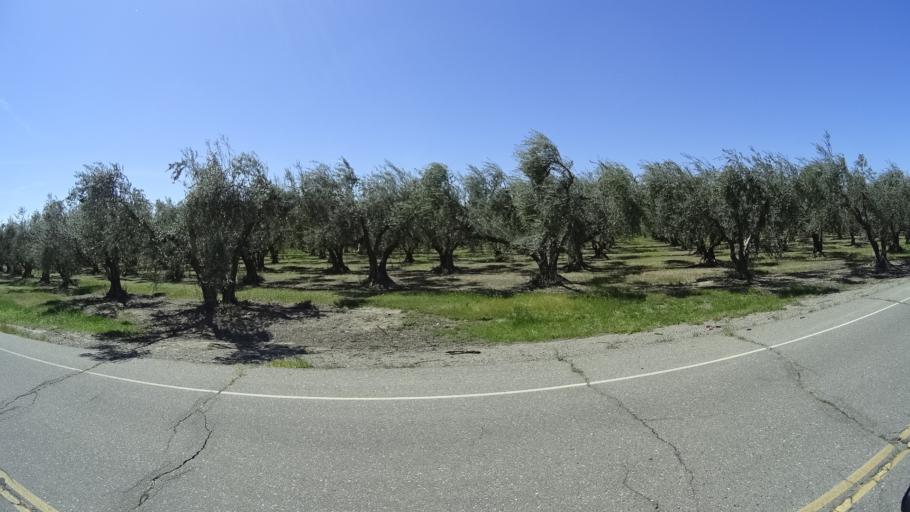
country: US
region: California
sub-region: Glenn County
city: Orland
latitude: 39.7462
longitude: -122.1596
